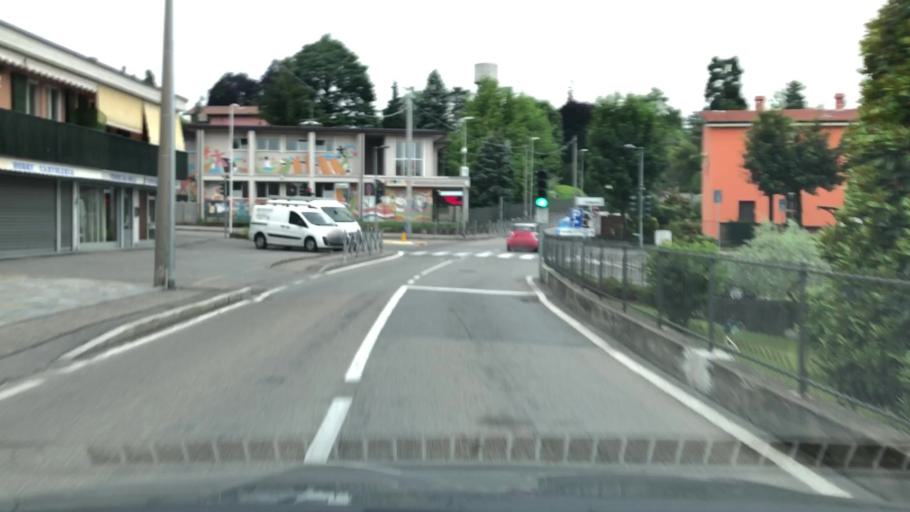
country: IT
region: Lombardy
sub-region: Provincia di Como
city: Casnate Con Bernate
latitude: 45.7613
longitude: 9.0756
